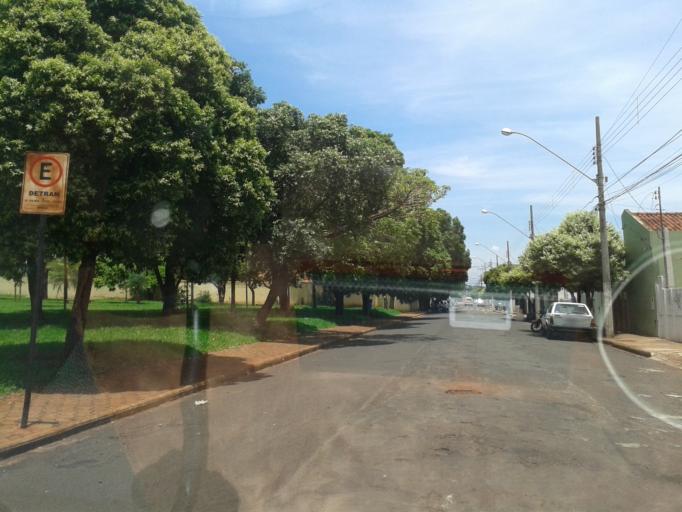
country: BR
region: Minas Gerais
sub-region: Ituiutaba
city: Ituiutaba
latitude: -18.9810
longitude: -49.4634
